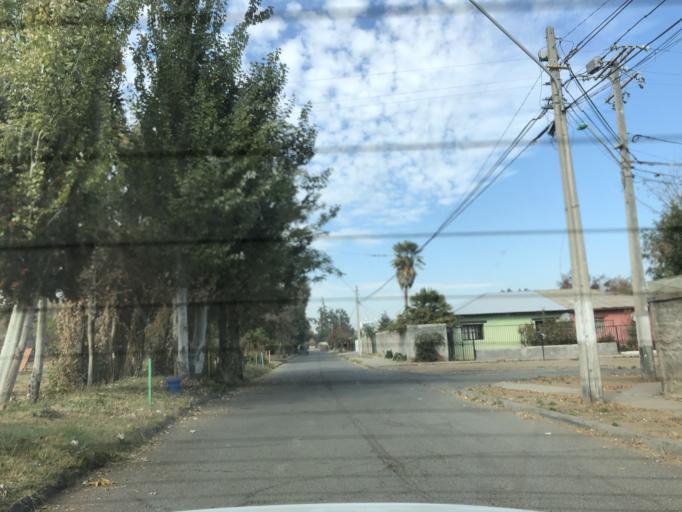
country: CL
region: Santiago Metropolitan
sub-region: Provincia de Cordillera
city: Puente Alto
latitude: -33.5755
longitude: -70.5524
